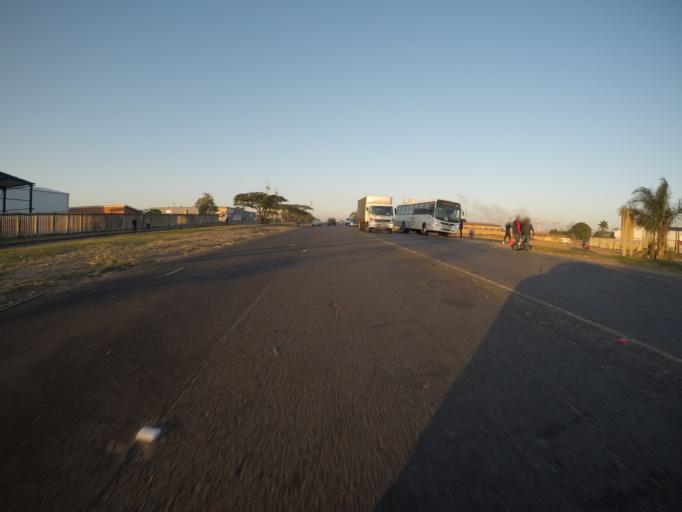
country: ZA
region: KwaZulu-Natal
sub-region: uThungulu District Municipality
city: Empangeni
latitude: -28.7796
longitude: 31.8990
